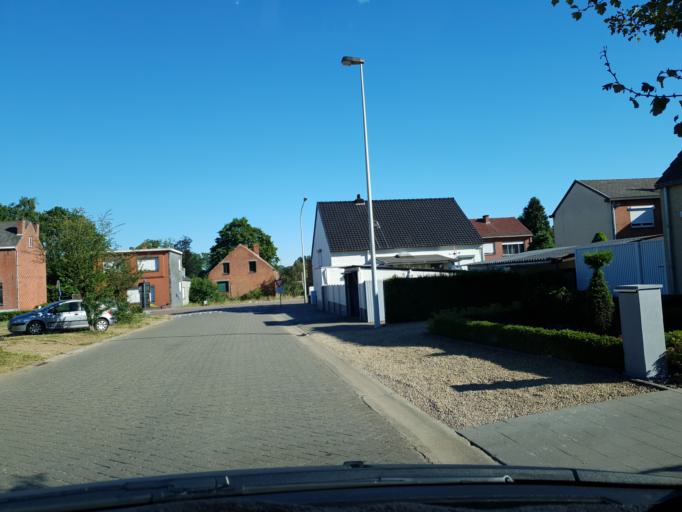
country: BE
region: Flanders
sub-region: Provincie Antwerpen
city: Grobbendonk
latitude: 51.1945
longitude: 4.7431
